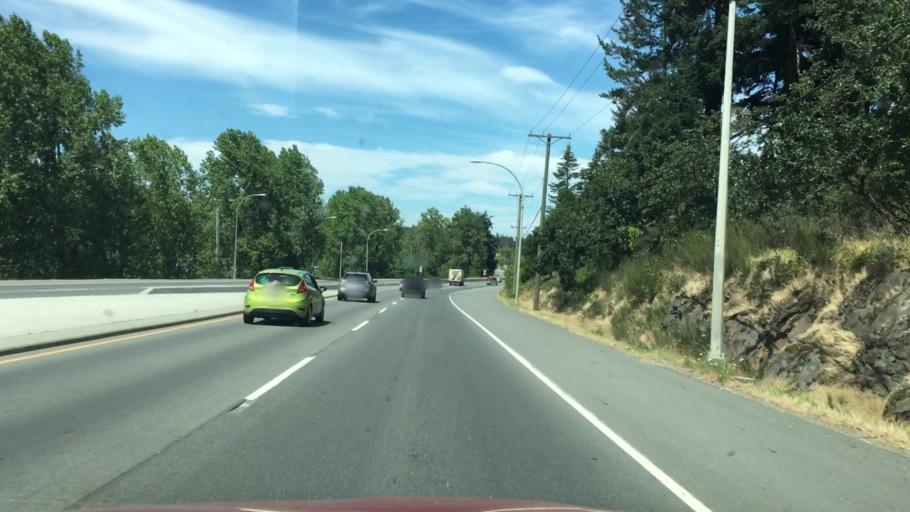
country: CA
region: British Columbia
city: Victoria
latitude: 48.5236
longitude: -123.3863
